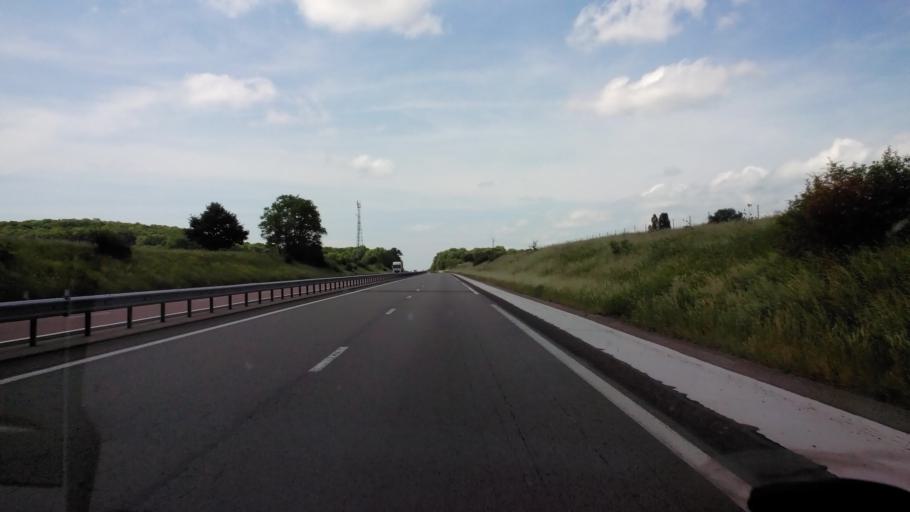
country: FR
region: Champagne-Ardenne
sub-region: Departement de la Haute-Marne
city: Saulxures
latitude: 48.0702
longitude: 5.5949
